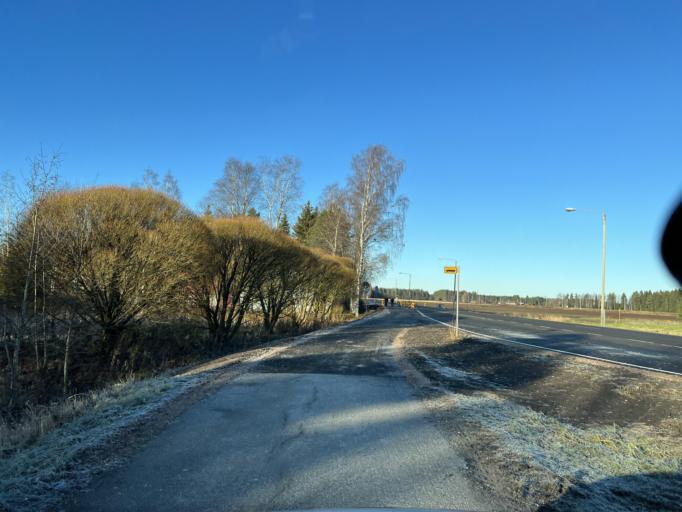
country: FI
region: Northern Ostrobothnia
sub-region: Nivala-Haapajaervi
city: Nivala
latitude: 63.9477
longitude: 24.9256
